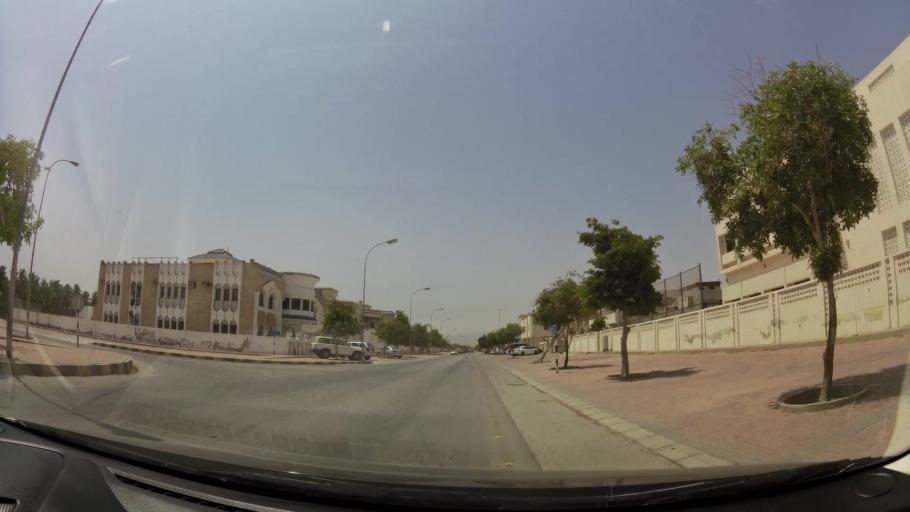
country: OM
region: Zufar
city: Salalah
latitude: 17.0146
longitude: 54.0757
